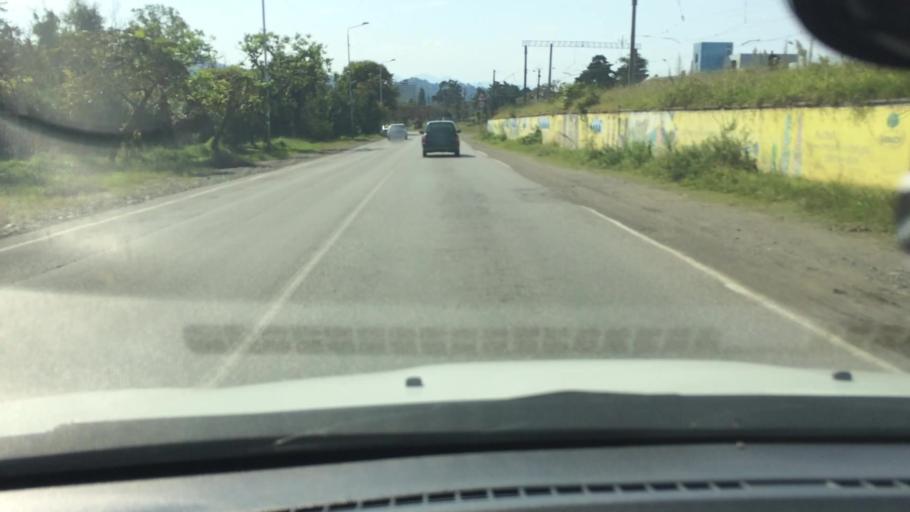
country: GE
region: Ajaria
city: Makhinjauri
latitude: 41.7320
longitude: 41.7321
